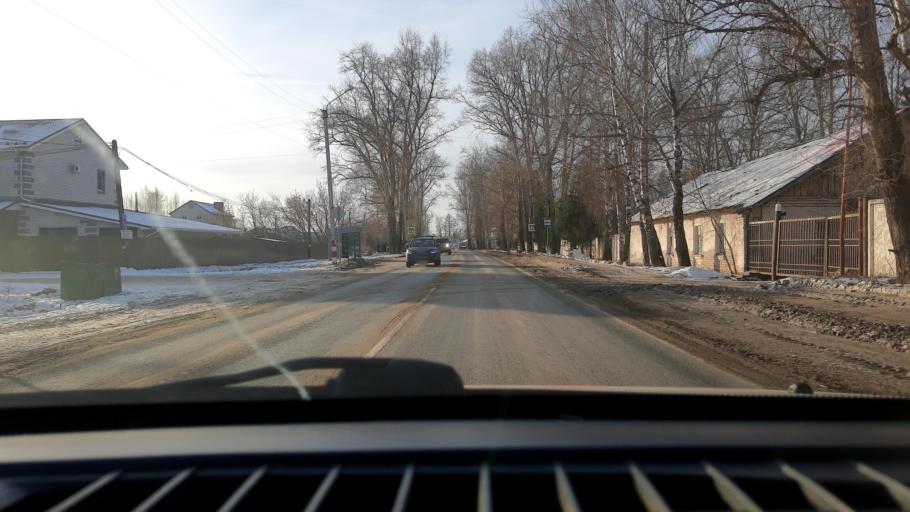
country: RU
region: Nizjnij Novgorod
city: Bor
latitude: 56.3814
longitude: 44.0349
